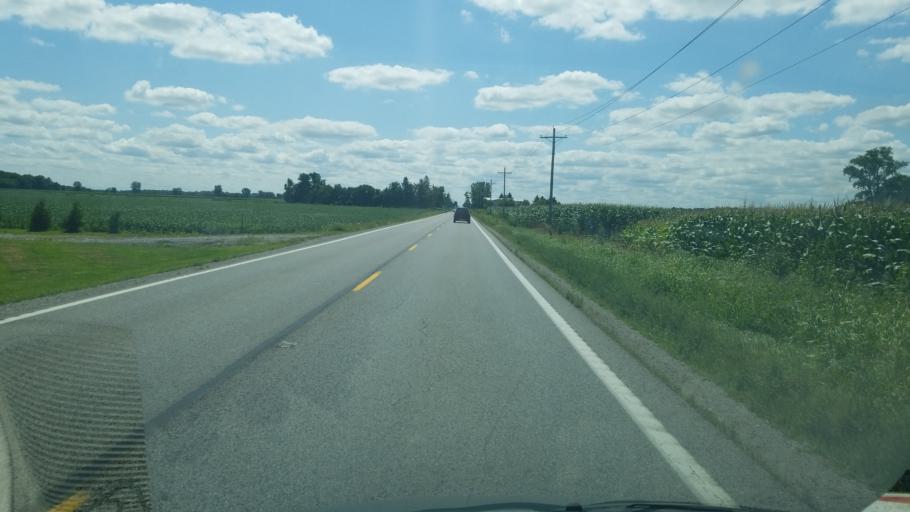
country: US
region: Ohio
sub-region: Fulton County
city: Delta
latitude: 41.6609
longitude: -84.0357
